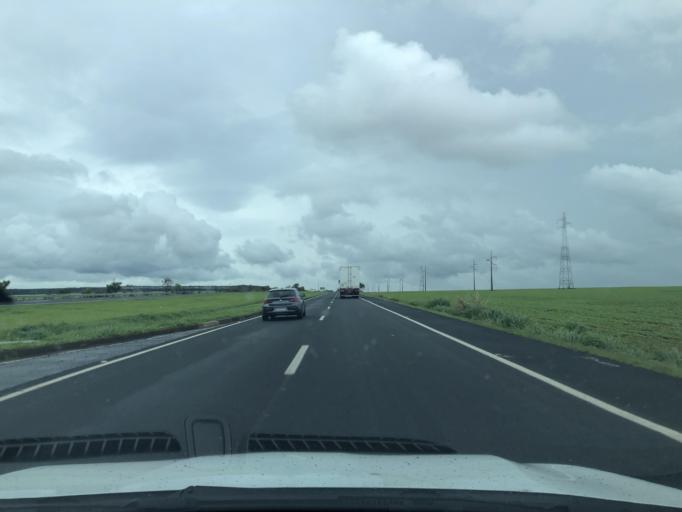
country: BR
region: Minas Gerais
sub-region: Uberlandia
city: Uberlandia
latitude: -19.0451
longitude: -48.1985
